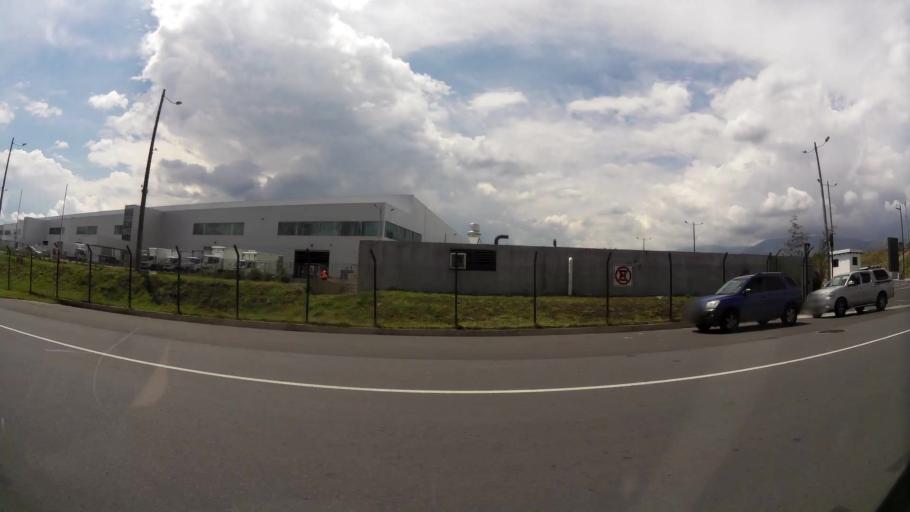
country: EC
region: Pichincha
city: Quito
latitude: -0.1537
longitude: -78.3499
